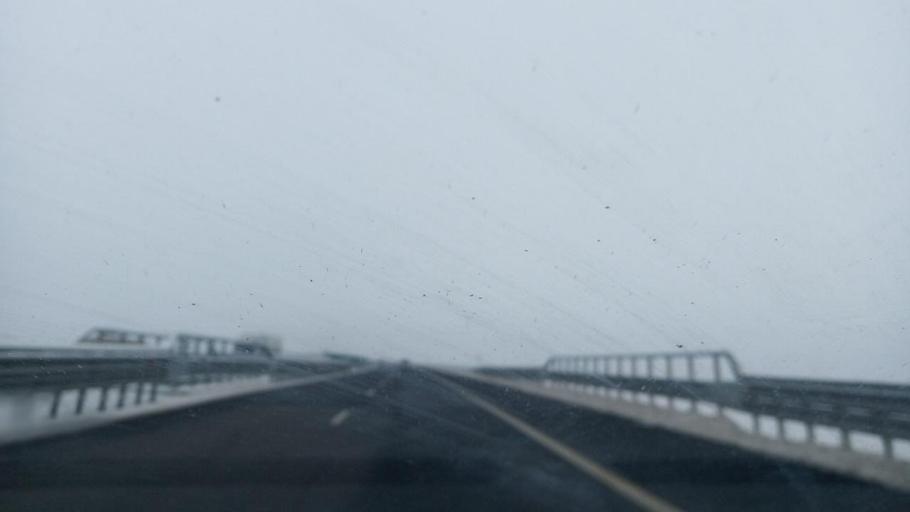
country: RO
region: Bacau
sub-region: Comuna Saucesti
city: Saucesti
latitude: 46.6102
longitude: 26.9587
